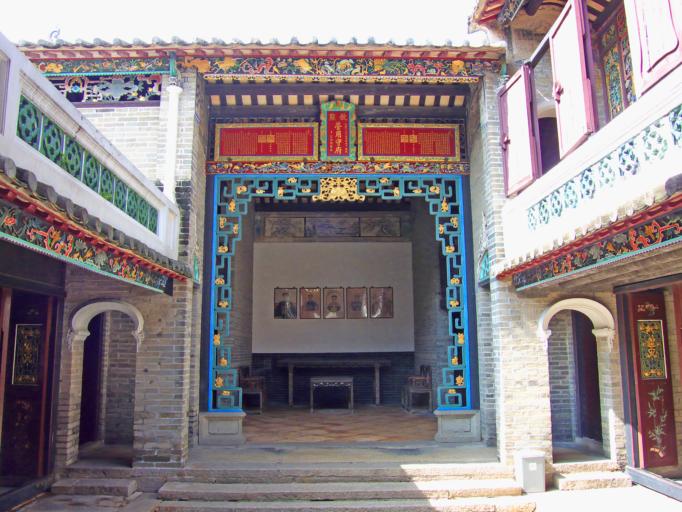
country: CN
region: Guangdong
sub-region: Shenzhen
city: Shenzhen
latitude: 22.4997
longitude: 114.0765
